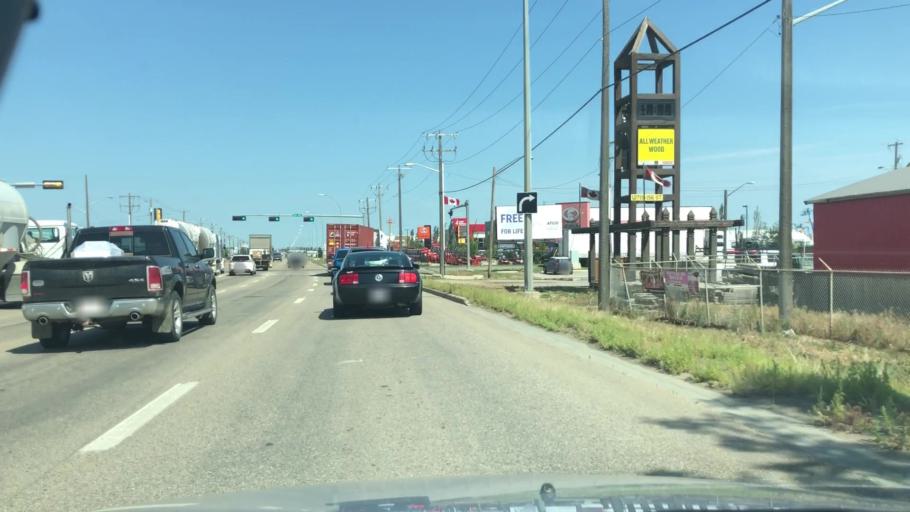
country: CA
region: Alberta
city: St. Albert
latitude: 53.5840
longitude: -113.5902
